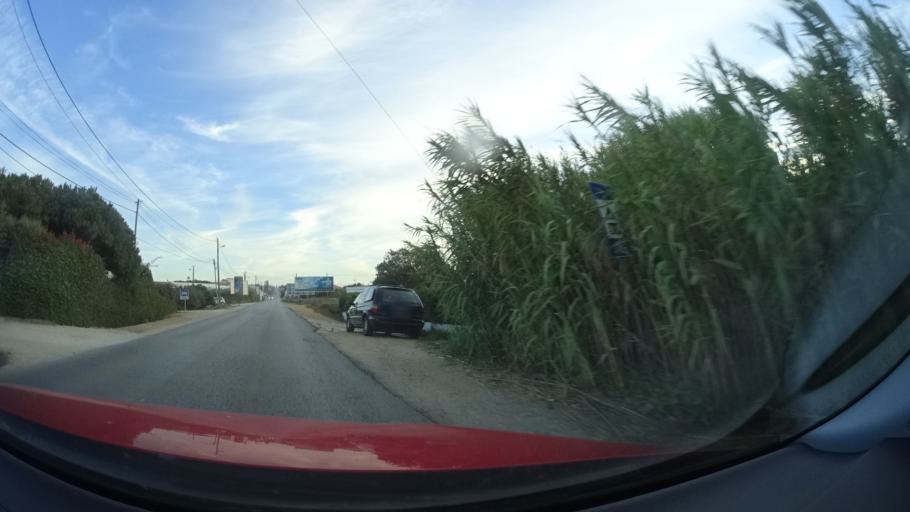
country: PT
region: Faro
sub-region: Vila do Bispo
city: Sagres
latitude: 37.0186
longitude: -8.9400
